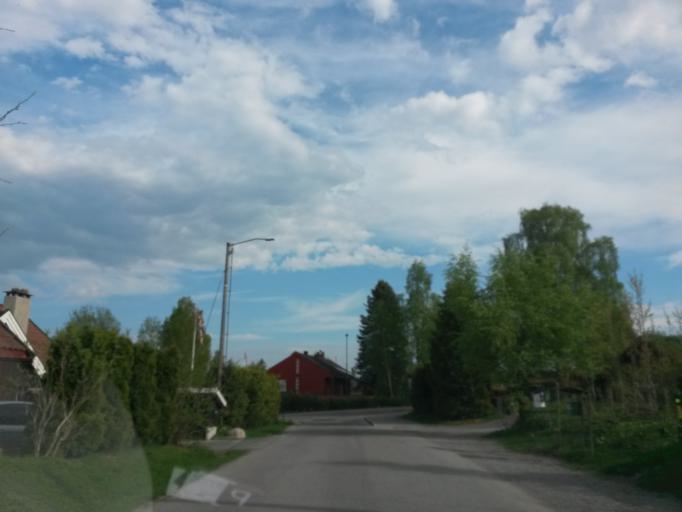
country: NO
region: Akershus
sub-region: Asker
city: Asker
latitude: 59.8331
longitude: 10.4091
